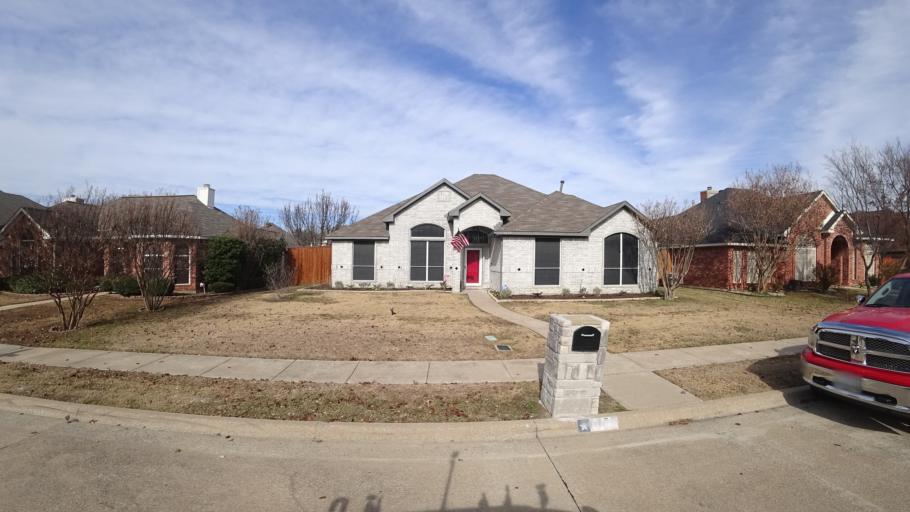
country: US
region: Texas
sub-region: Denton County
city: Highland Village
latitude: 33.0630
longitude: -97.0434
